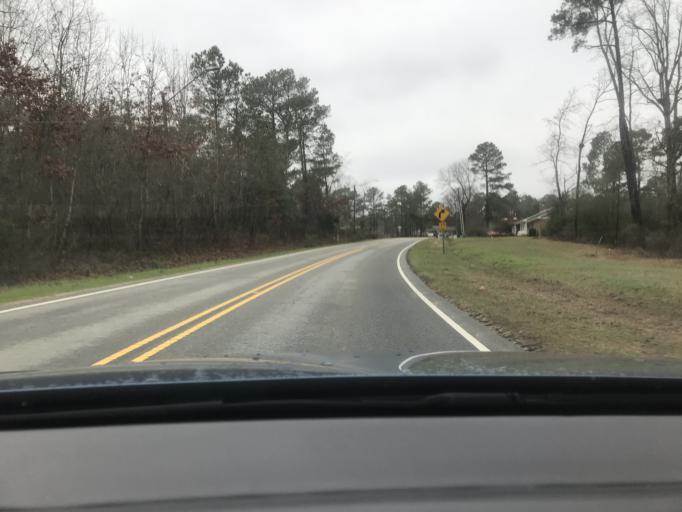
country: US
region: North Carolina
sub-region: Hoke County
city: Rockfish
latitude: 35.0231
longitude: -79.0095
